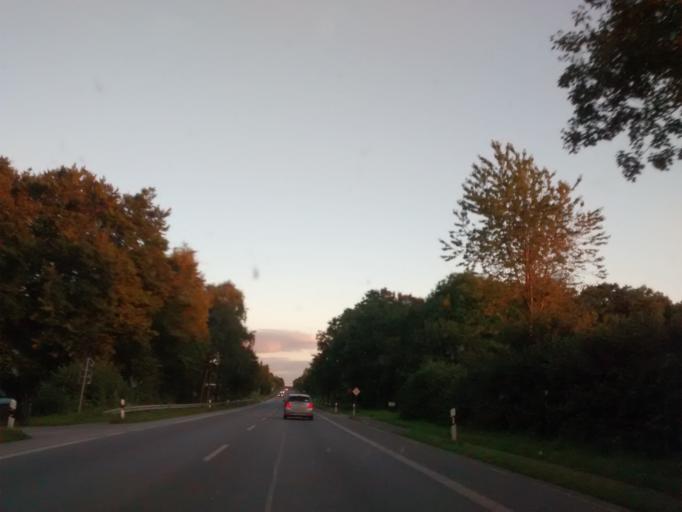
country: DE
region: North Rhine-Westphalia
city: Halle
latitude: 52.0434
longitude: 8.3869
